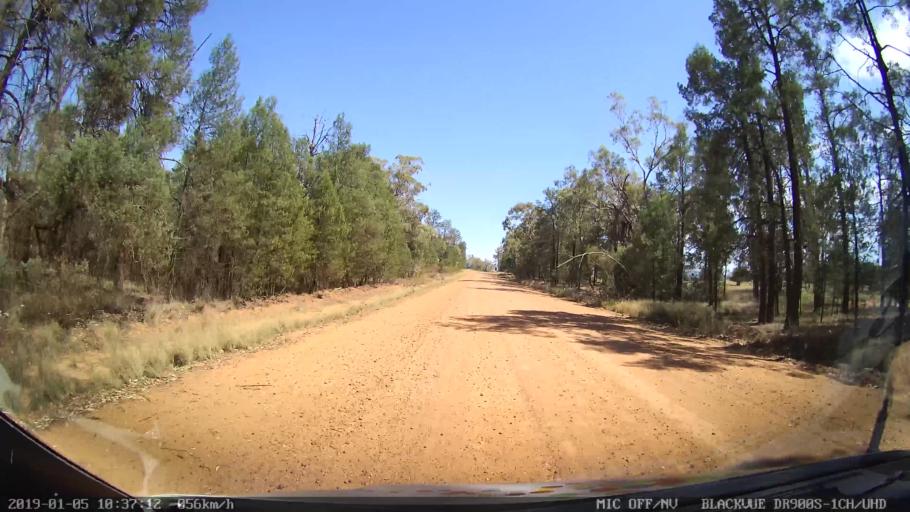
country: AU
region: New South Wales
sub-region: Gilgandra
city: Gilgandra
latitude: -31.4764
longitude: 148.9224
